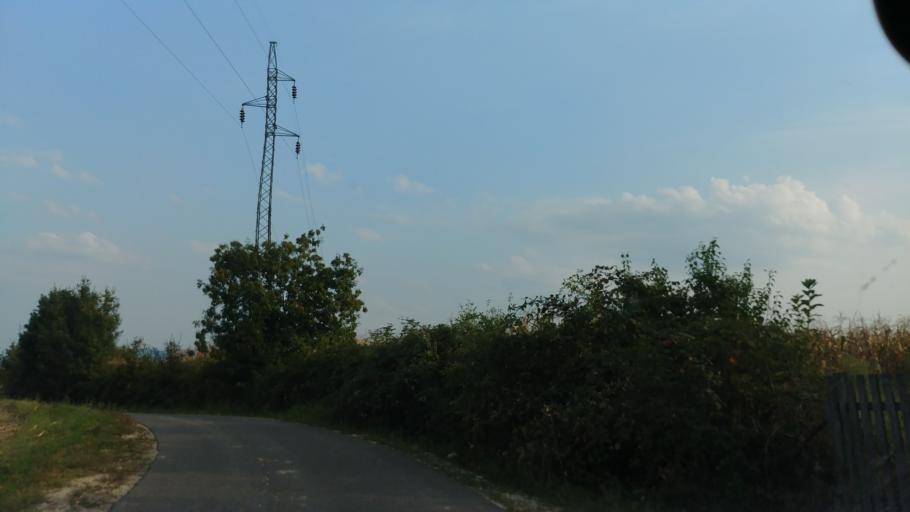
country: BA
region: Republika Srpska
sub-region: Opstina Ugljevik
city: Ugljevik
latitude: 44.7079
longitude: 19.0058
